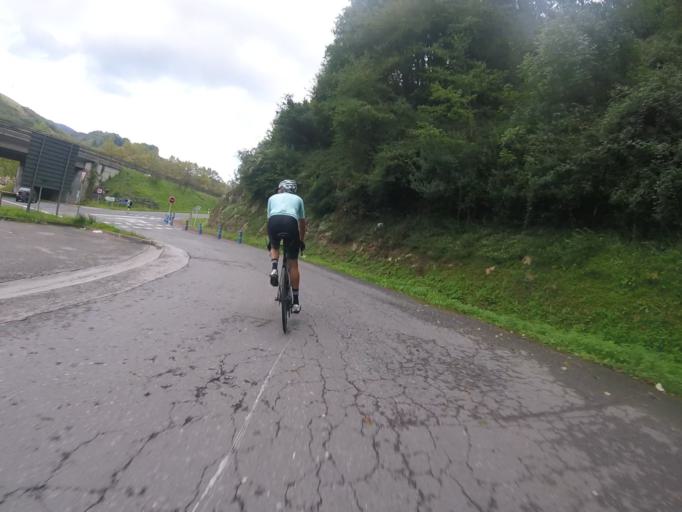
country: ES
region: Basque Country
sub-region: Provincia de Guipuzcoa
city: Tolosa
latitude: 43.1228
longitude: -2.0876
